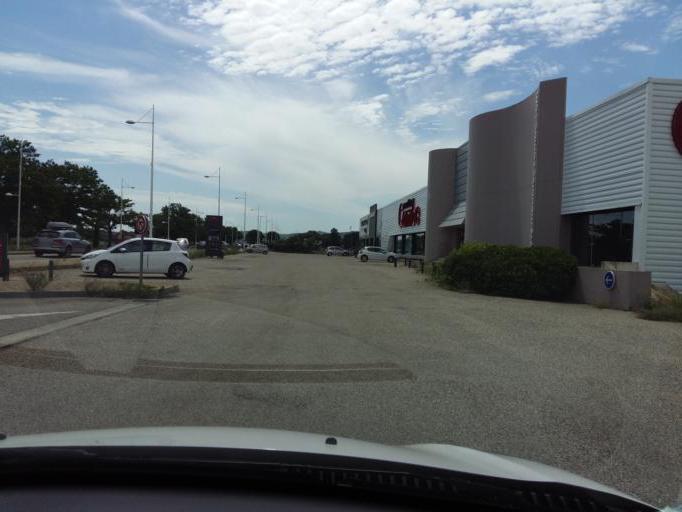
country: FR
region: Provence-Alpes-Cote d'Azur
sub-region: Departement du Vaucluse
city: Bollene
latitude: 44.3008
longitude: 4.7479
